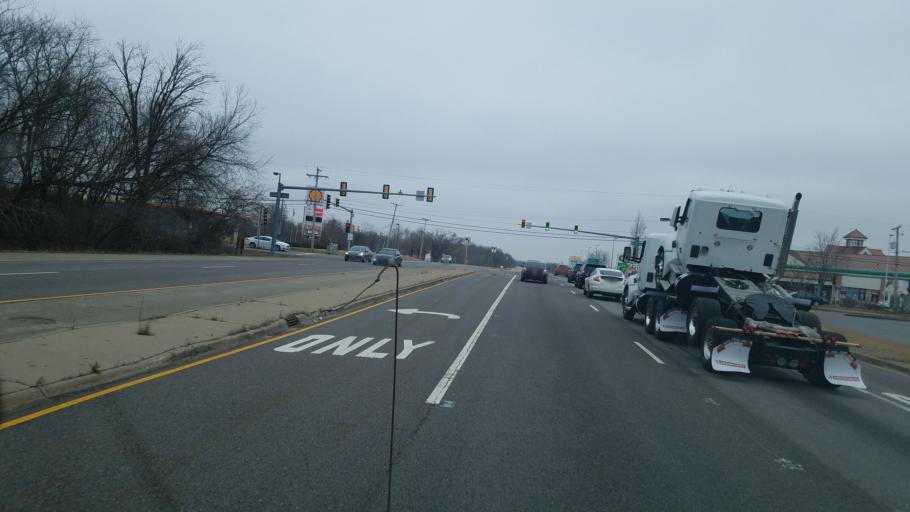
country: US
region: Illinois
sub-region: Lake County
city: Wadsworth
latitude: 42.4283
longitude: -87.9380
